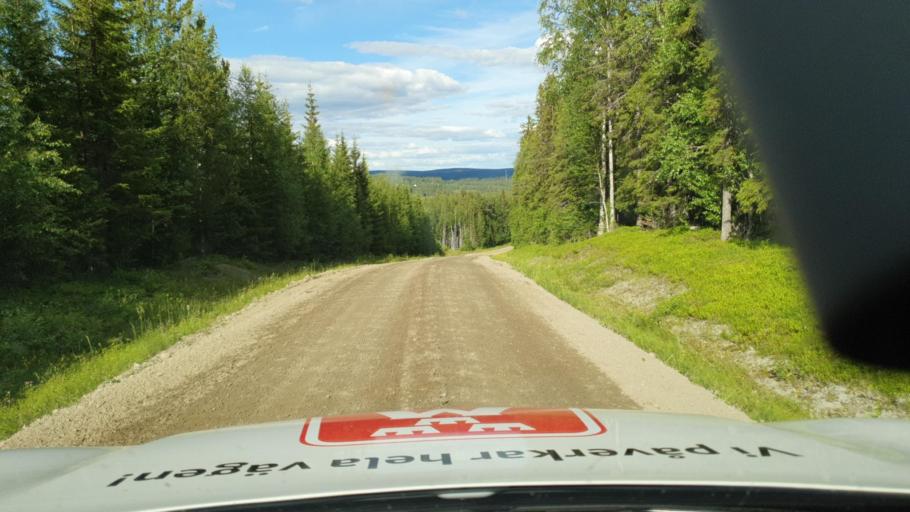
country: SE
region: Vaesterbotten
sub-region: Lycksele Kommun
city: Lycksele
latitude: 64.3628
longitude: 18.5435
